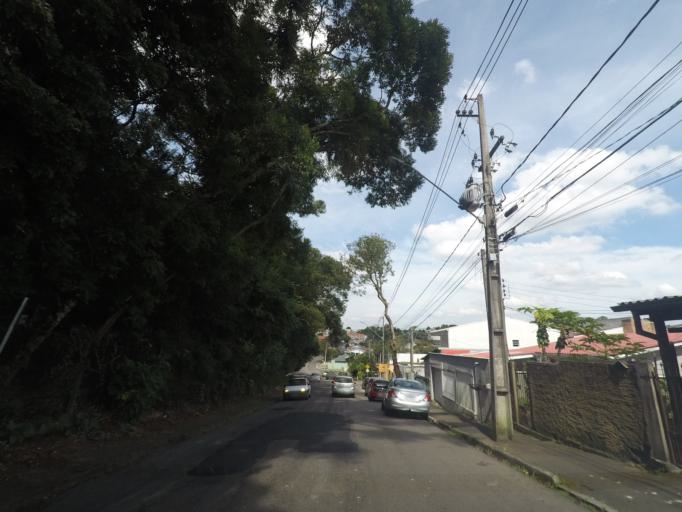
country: BR
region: Parana
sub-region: Curitiba
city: Curitiba
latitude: -25.4903
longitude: -49.2629
